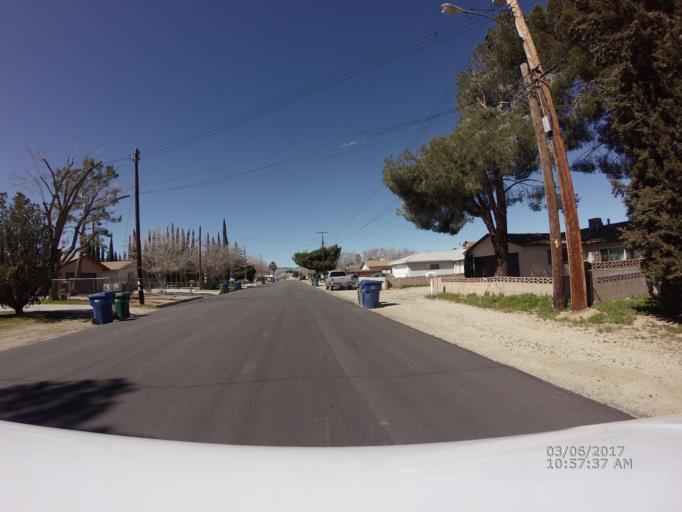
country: US
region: California
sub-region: Los Angeles County
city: Quartz Hill
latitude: 34.6584
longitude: -118.2253
